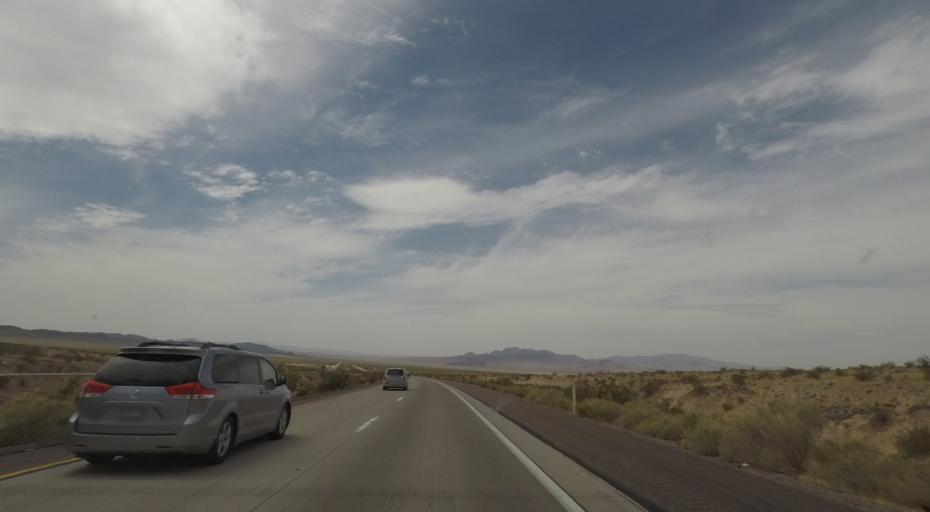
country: US
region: California
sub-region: San Bernardino County
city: Twentynine Palms
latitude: 34.7276
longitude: -116.0814
